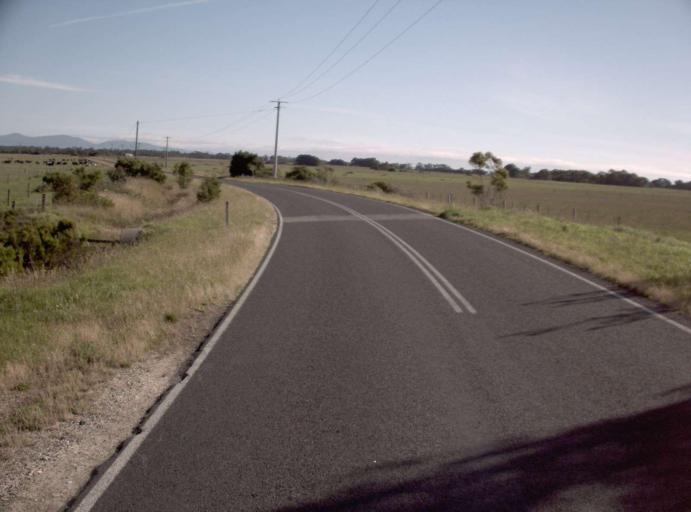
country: AU
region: Victoria
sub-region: Latrobe
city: Morwell
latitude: -38.6796
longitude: 146.3906
